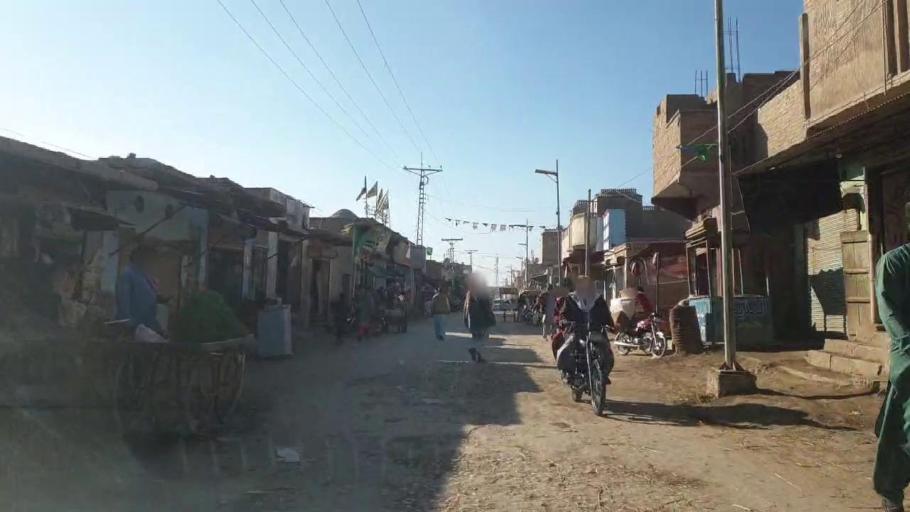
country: PK
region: Sindh
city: New Badah
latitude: 27.3285
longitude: 68.0255
